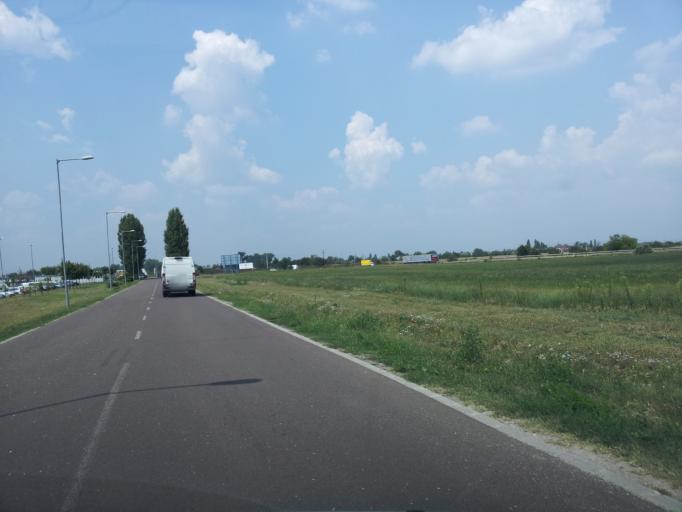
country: HU
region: Pest
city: Taksony
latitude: 47.3077
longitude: 19.0459
